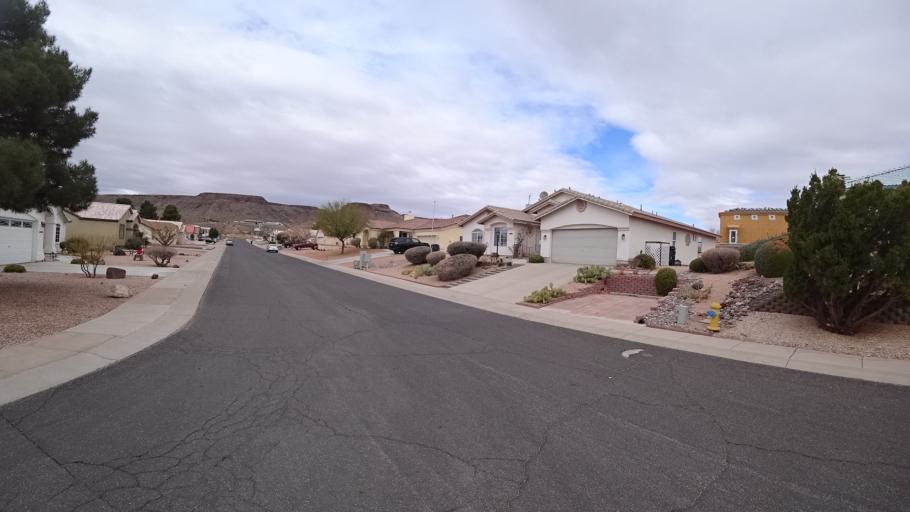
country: US
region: Arizona
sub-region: Mohave County
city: New Kingman-Butler
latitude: 35.2395
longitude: -114.0465
